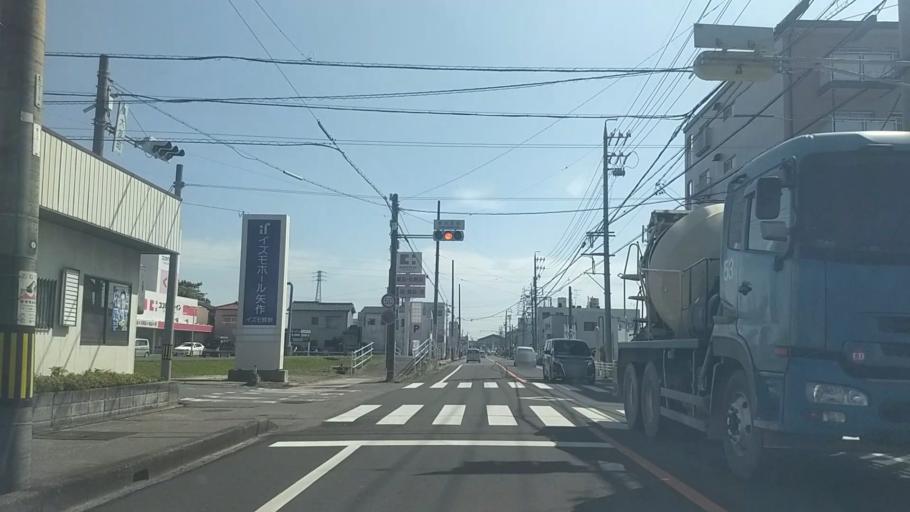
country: JP
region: Aichi
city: Okazaki
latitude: 34.9723
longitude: 137.1333
